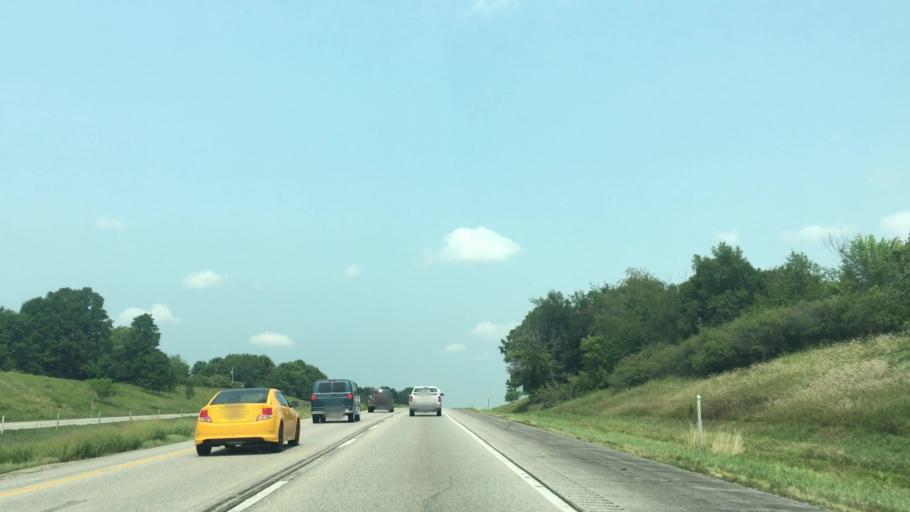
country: US
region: Iowa
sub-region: Linn County
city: Ely
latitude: 41.8311
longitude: -91.6607
